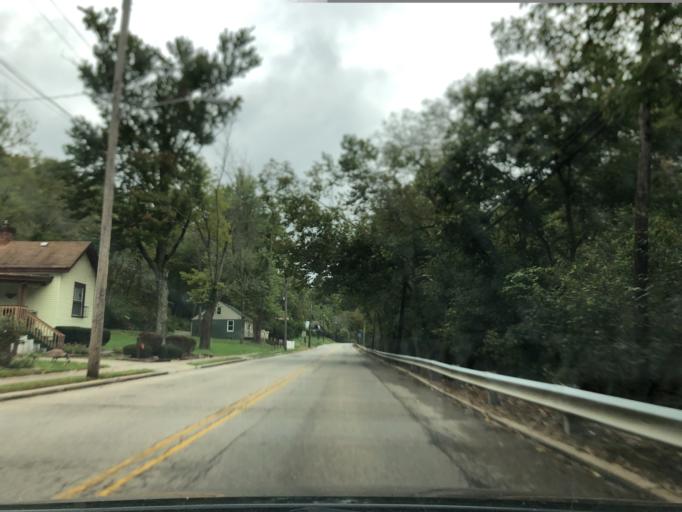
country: US
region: Ohio
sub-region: Hamilton County
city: Mariemont
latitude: 39.1614
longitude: -84.3809
